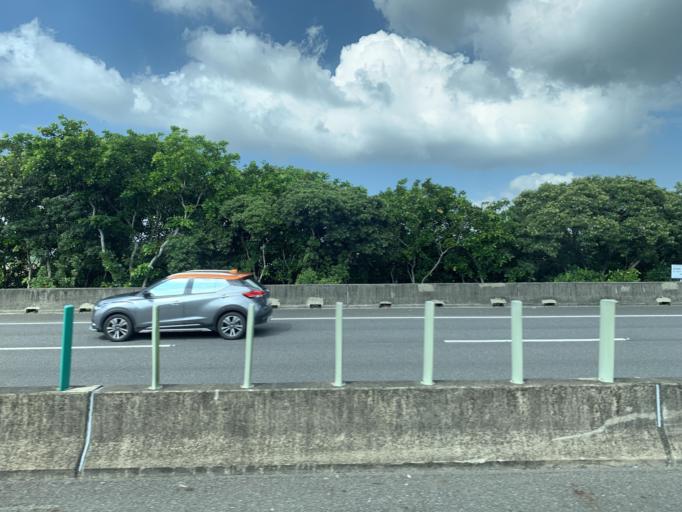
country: TW
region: Taiwan
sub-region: Pingtung
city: Pingtung
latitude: 22.8636
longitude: 120.4914
